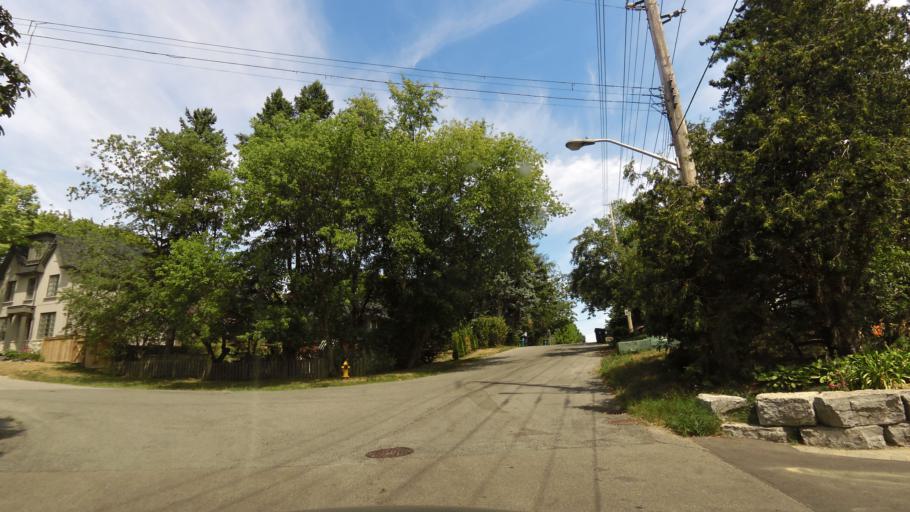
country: CA
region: Ontario
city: Etobicoke
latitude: 43.6345
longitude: -79.5009
